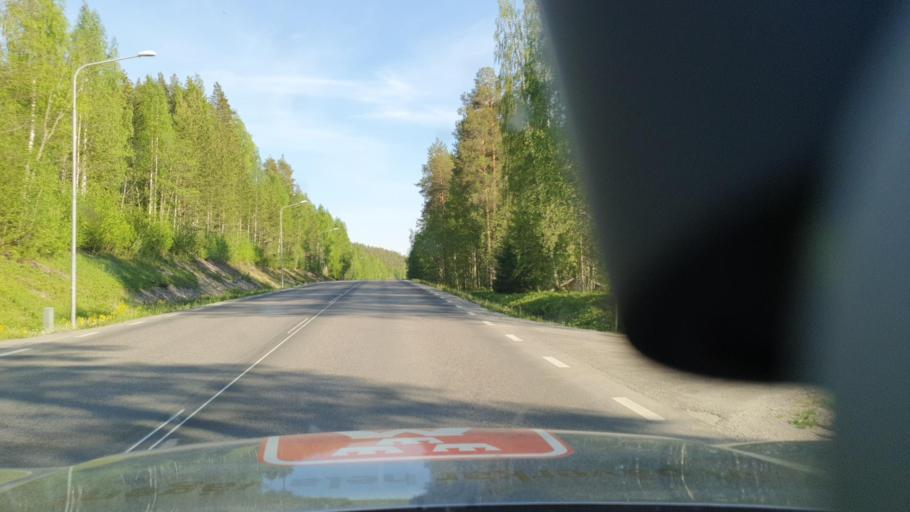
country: SE
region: Norrbotten
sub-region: Bodens Kommun
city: Boden
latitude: 65.8427
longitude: 21.6035
